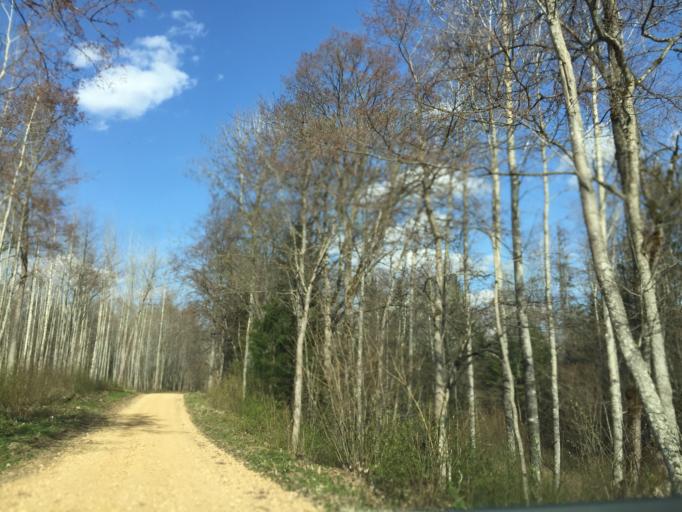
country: LV
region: Skriveri
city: Skriveri
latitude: 56.8005
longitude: 25.2233
